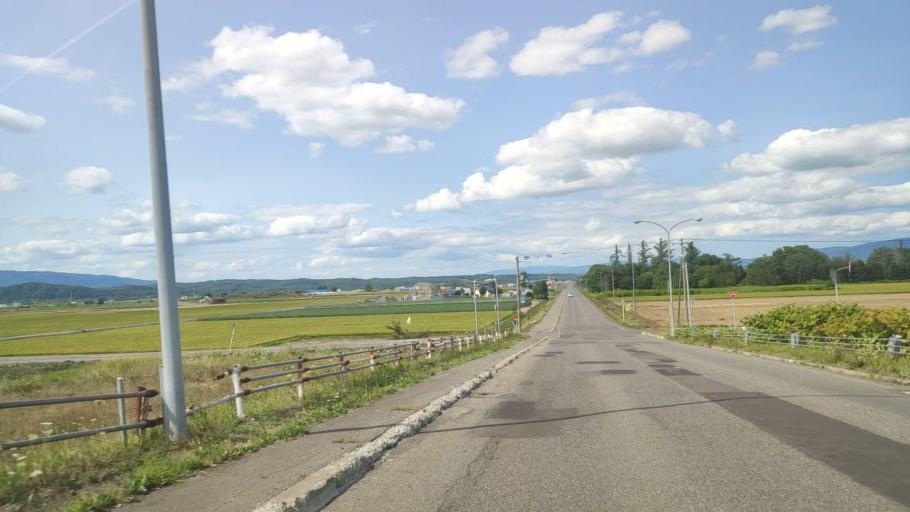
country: JP
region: Hokkaido
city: Nayoro
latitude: 44.3006
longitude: 142.4294
